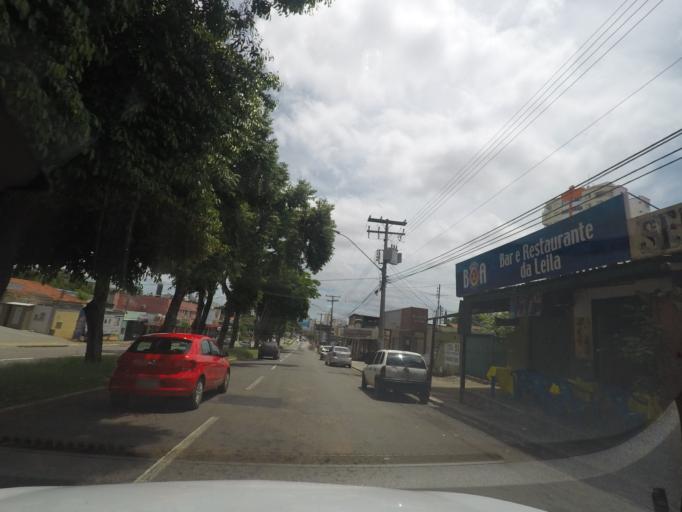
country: BR
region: Goias
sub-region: Goiania
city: Goiania
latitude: -16.6874
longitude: -49.2437
